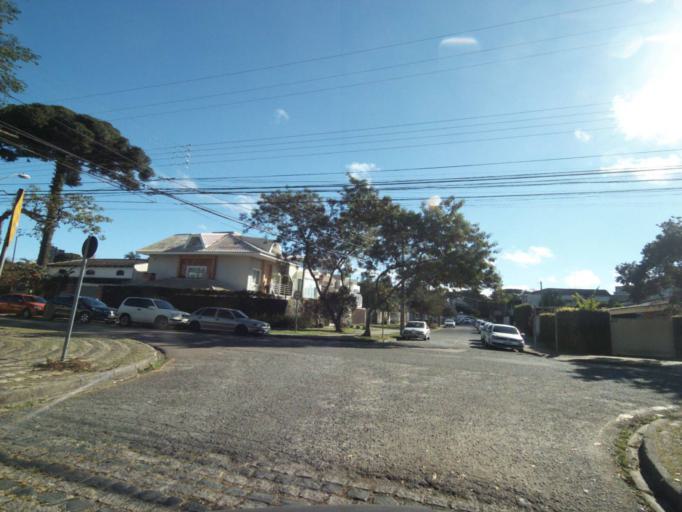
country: BR
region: Parana
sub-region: Curitiba
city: Curitiba
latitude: -25.4187
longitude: -49.2493
